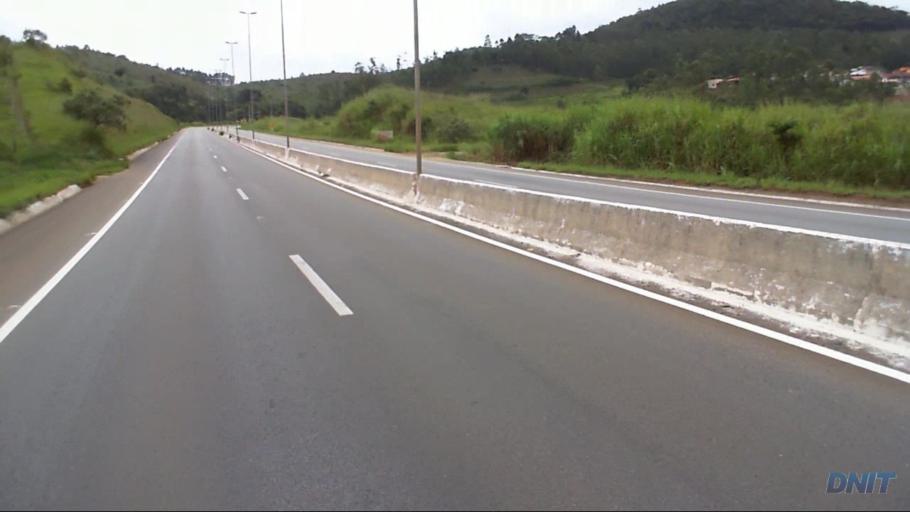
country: BR
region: Minas Gerais
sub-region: Nova Era
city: Nova Era
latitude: -19.7660
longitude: -43.0473
